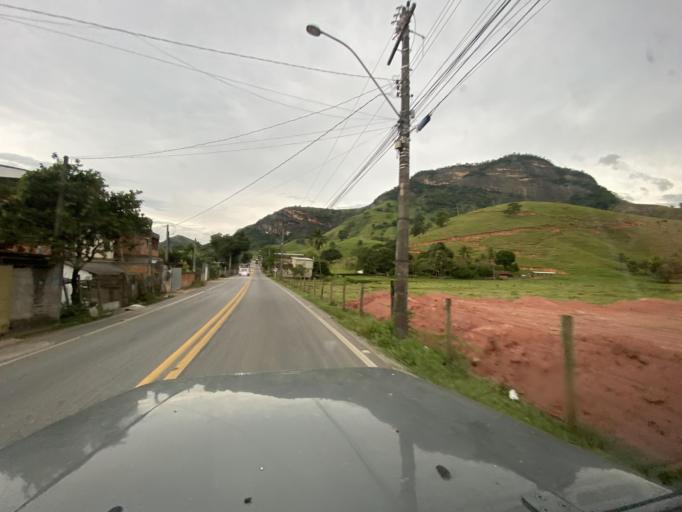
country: BR
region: Espirito Santo
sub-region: Jeronimo Monteiro
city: Jeronimo Monteiro
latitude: -20.8035
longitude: -41.3590
